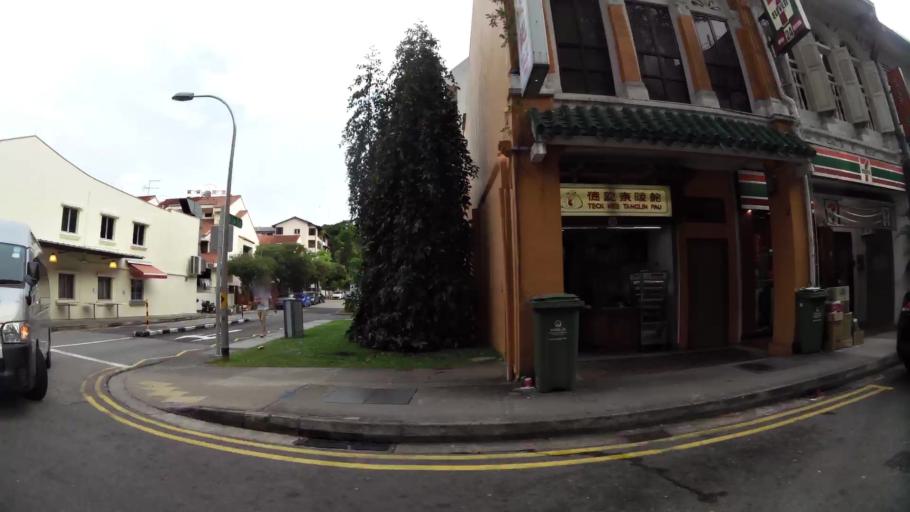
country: SG
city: Singapore
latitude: 1.2986
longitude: 103.8391
